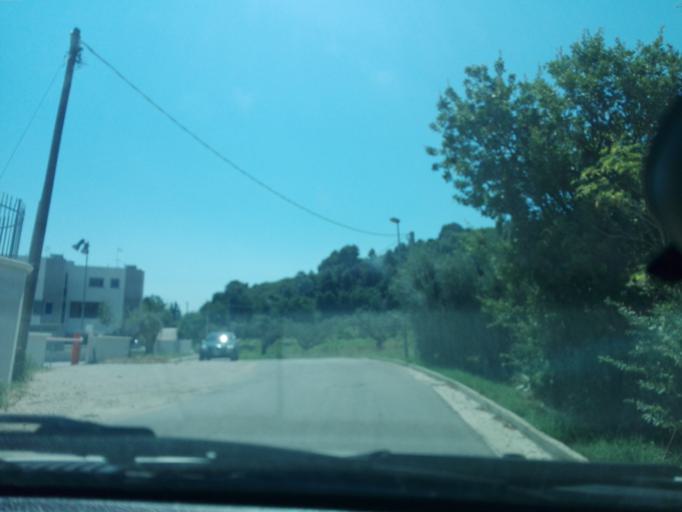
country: IT
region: Abruzzo
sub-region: Provincia di Pescara
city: Montesilvano Marina
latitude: 42.5006
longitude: 14.1570
